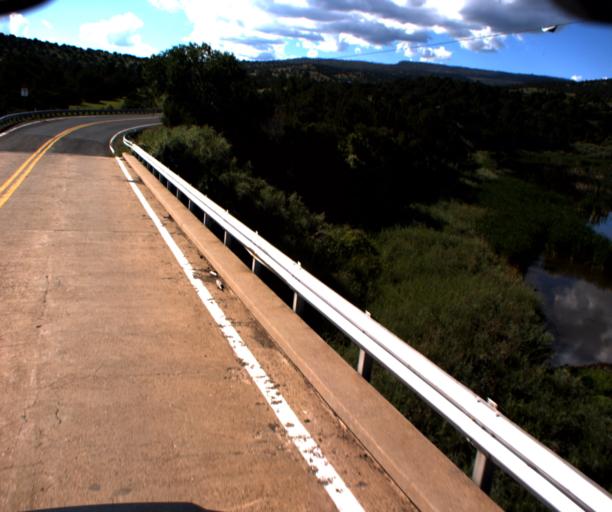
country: US
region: Arizona
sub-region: Apache County
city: Eagar
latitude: 34.1037
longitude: -109.3433
